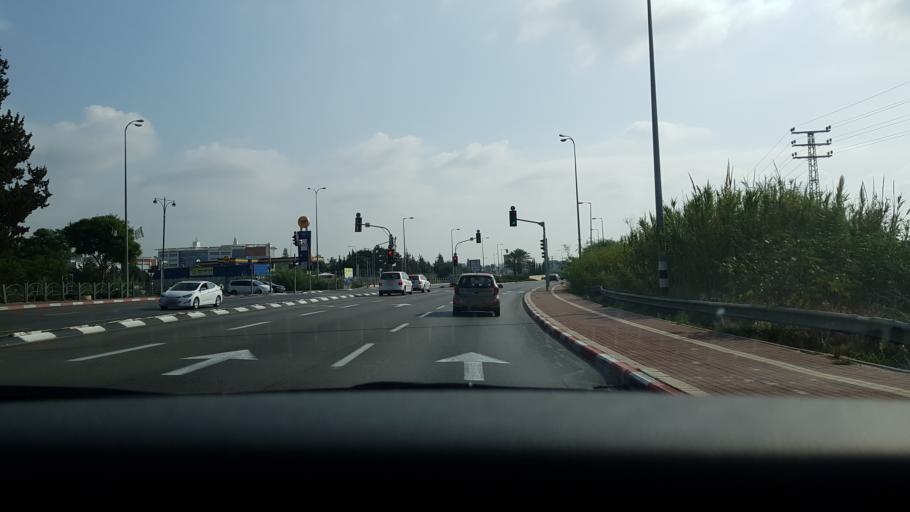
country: IL
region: Central District
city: Ness Ziona
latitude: 31.9219
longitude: 34.7844
